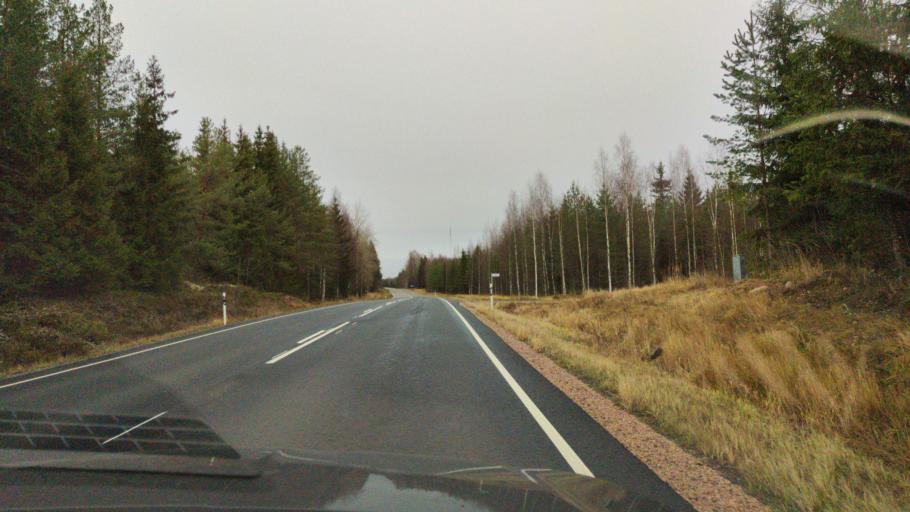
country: FI
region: Varsinais-Suomi
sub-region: Loimaa
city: Aura
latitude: 60.7143
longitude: 22.4443
